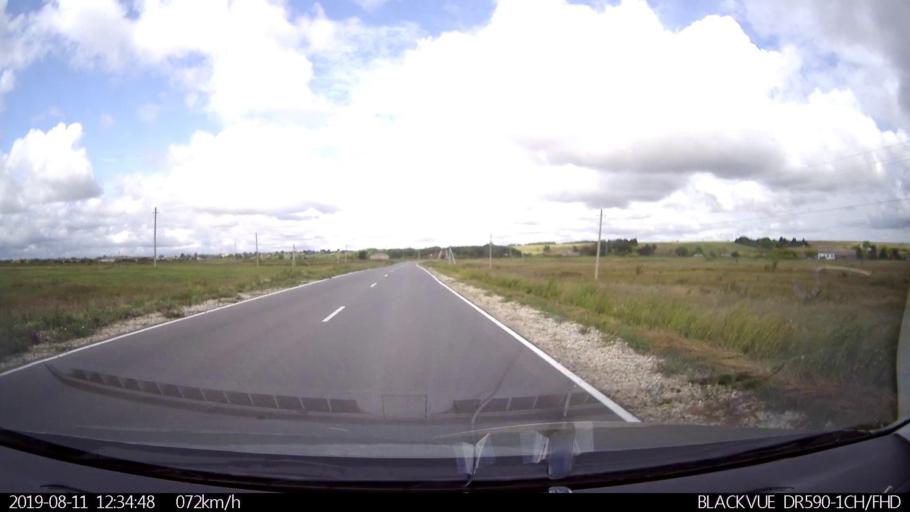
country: RU
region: Ulyanovsk
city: Ignatovka
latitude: 53.8196
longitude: 47.8380
